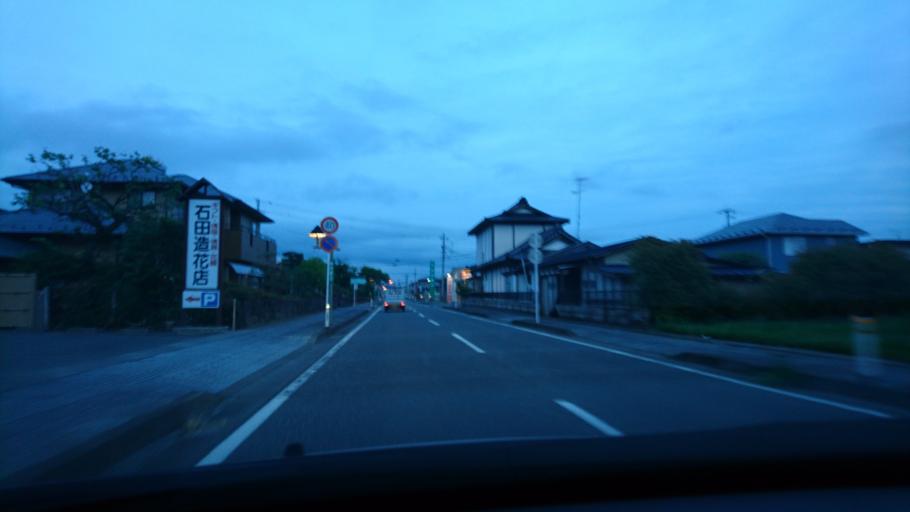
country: JP
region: Iwate
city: Ichinoseki
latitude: 38.8321
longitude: 140.9936
